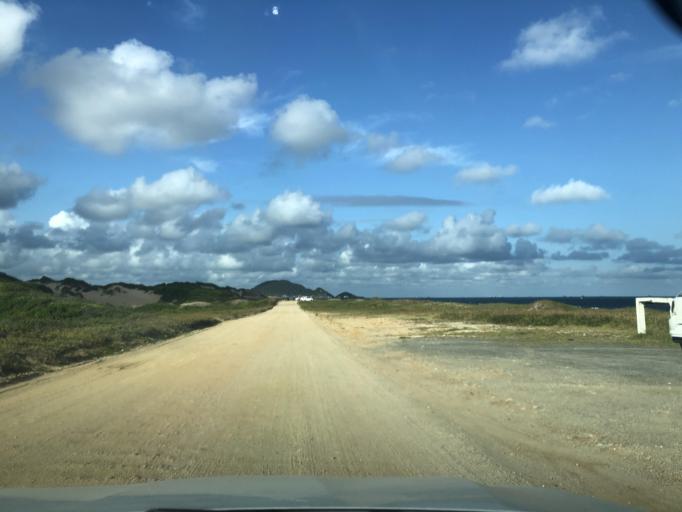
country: BR
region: Santa Catarina
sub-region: Sao Francisco Do Sul
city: Sao Francisco do Sul
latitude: -26.2550
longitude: -48.5157
